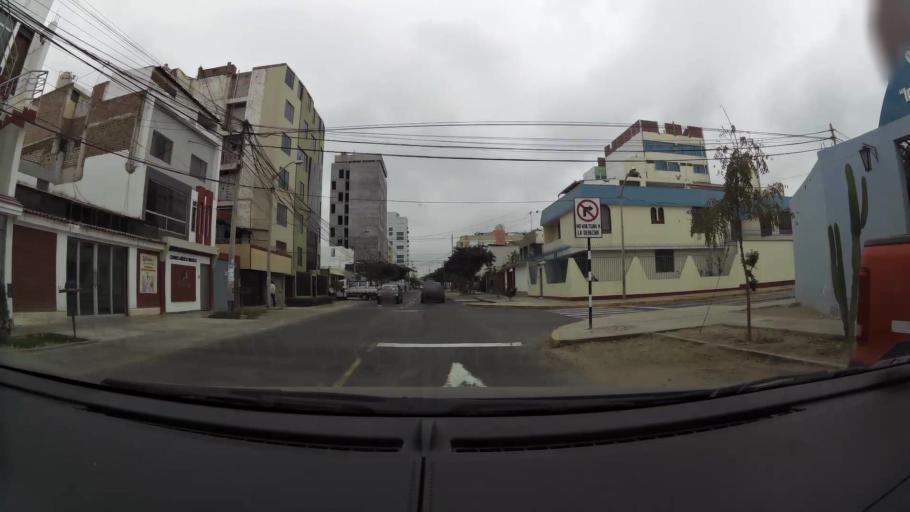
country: PE
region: La Libertad
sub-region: Provincia de Trujillo
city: Trujillo
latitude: -8.1206
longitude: -79.0375
